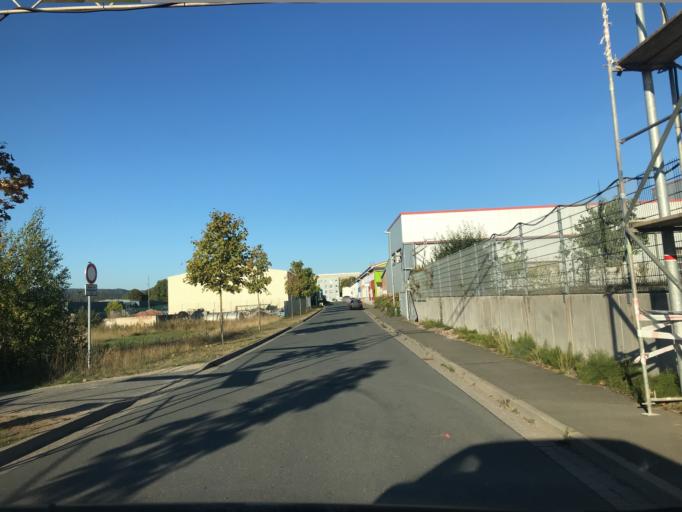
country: DE
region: Thuringia
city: Leinefelde
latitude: 51.3780
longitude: 10.3347
